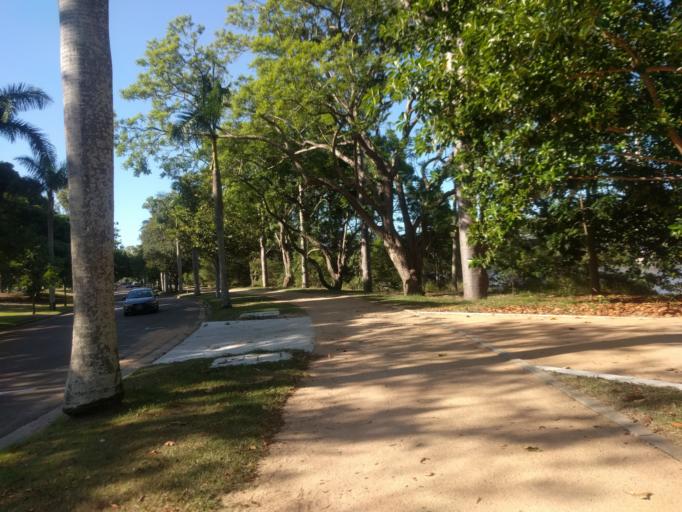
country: AU
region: Queensland
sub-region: Brisbane
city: Yeronga
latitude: -27.5002
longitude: 153.0202
